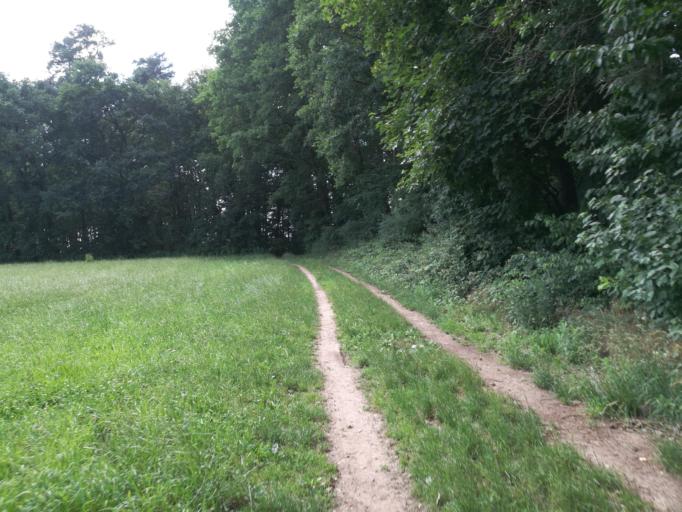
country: DE
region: Bavaria
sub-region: Regierungsbezirk Mittelfranken
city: Seukendorf
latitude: 49.4939
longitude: 10.8967
